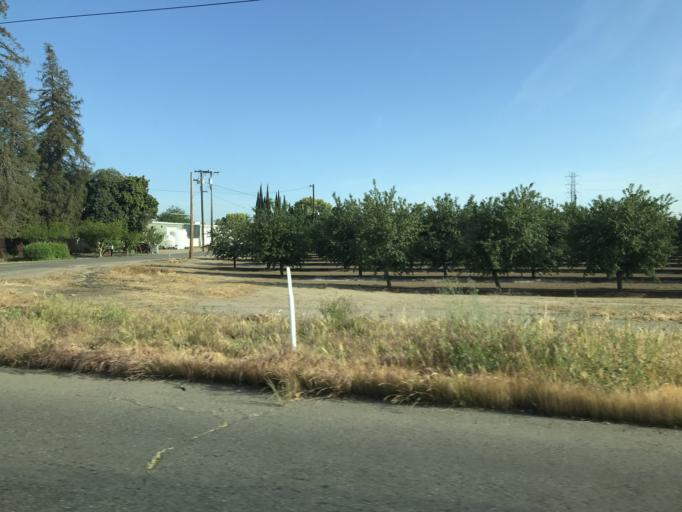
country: US
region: California
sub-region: Fresno County
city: West Park
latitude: 36.7354
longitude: -119.8985
